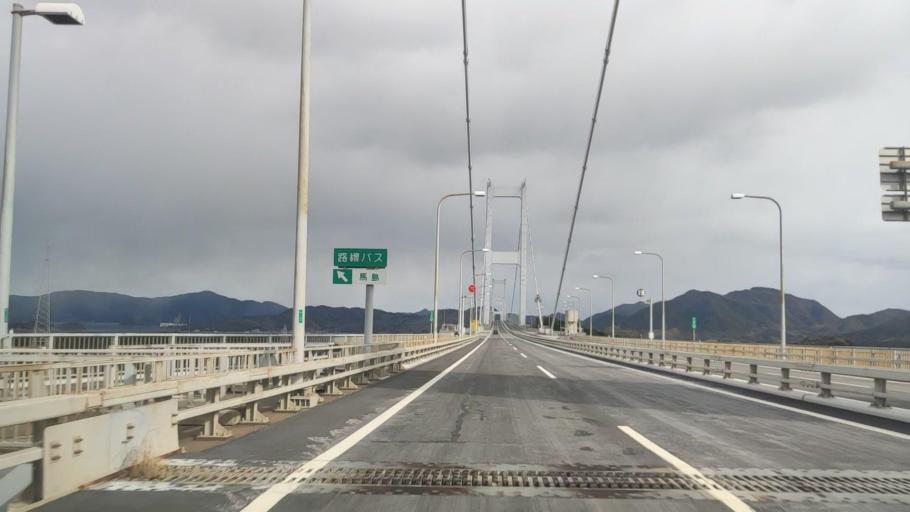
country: JP
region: Hiroshima
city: Takehara
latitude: 34.1172
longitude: 132.9893
